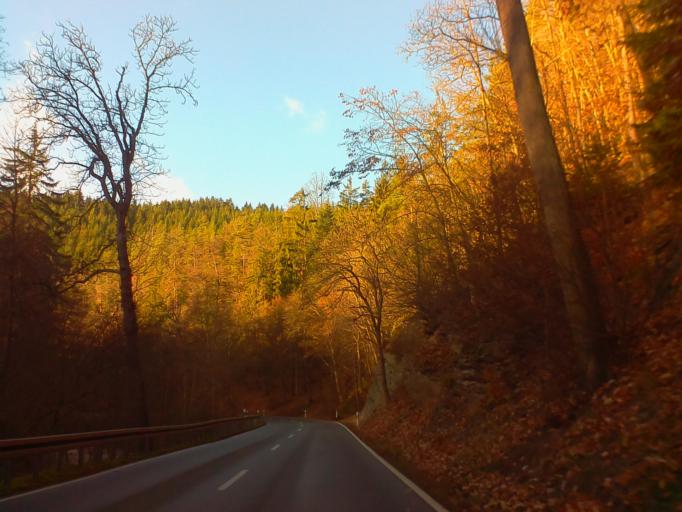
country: DE
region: Thuringia
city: Schwarzburg
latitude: 50.6637
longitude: 11.2184
